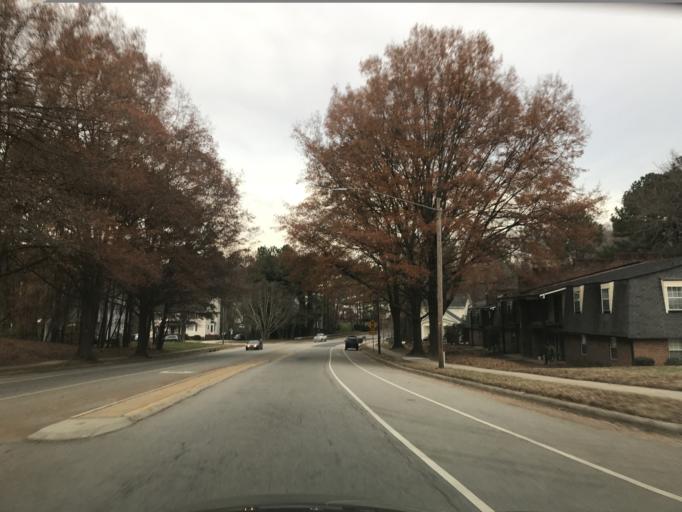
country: US
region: North Carolina
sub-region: Wake County
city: West Raleigh
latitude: 35.7715
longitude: -78.6938
